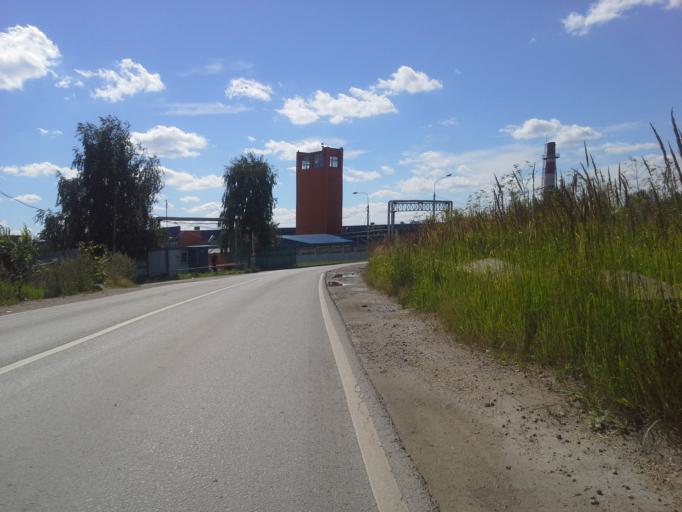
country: RU
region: Moscow
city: Solntsevo
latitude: 55.6593
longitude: 37.3780
